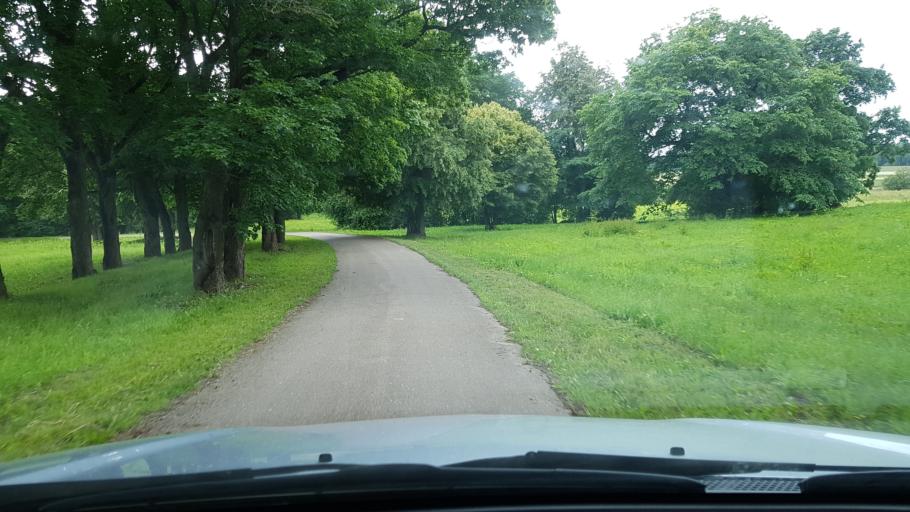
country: EE
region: Ida-Virumaa
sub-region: Narva-Joesuu linn
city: Narva-Joesuu
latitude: 59.3887
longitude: 27.9801
